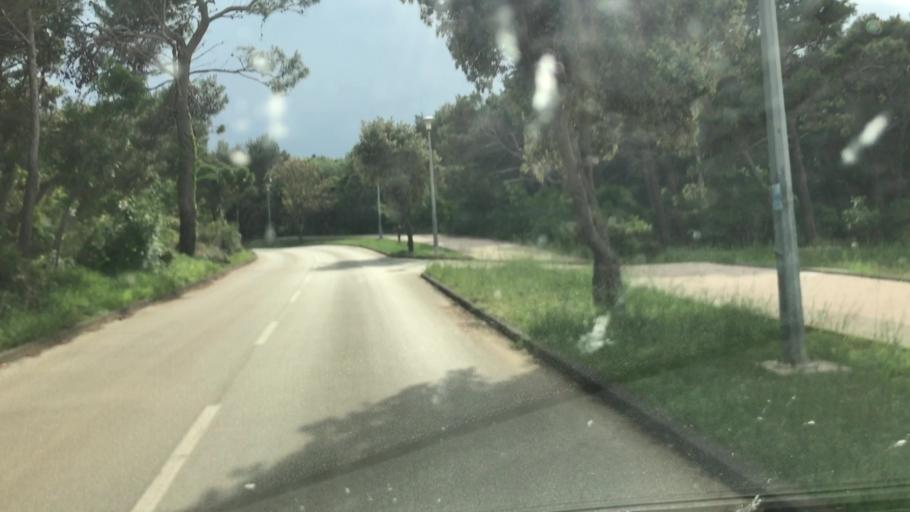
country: HR
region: Licko-Senjska
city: Novalja
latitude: 44.5462
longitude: 14.8827
